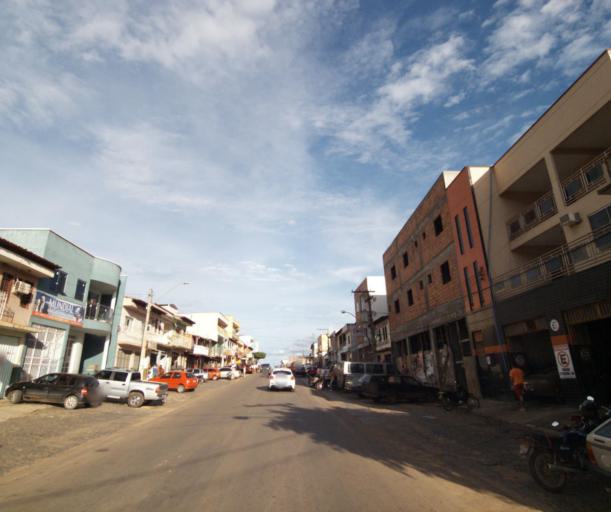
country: BR
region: Bahia
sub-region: Caetite
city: Caetite
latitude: -14.0654
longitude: -42.4835
